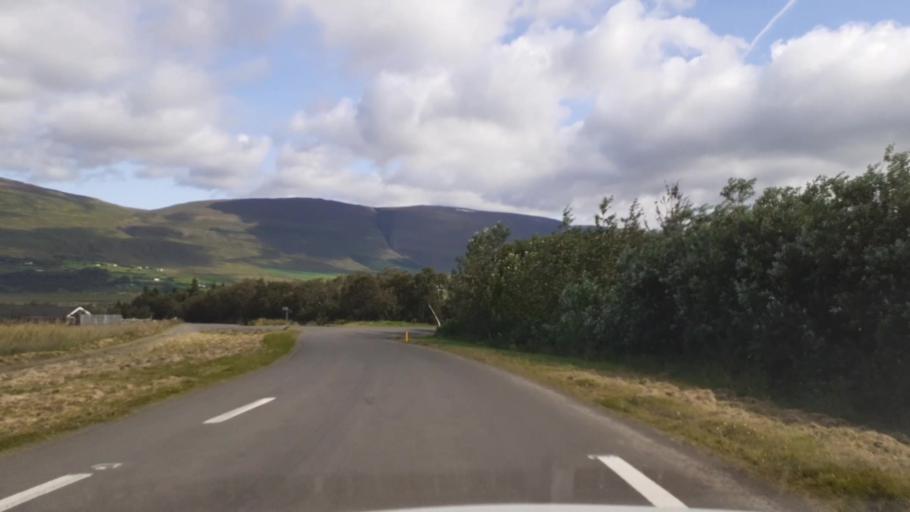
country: IS
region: Northeast
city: Akureyri
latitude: 65.6490
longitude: -18.0894
